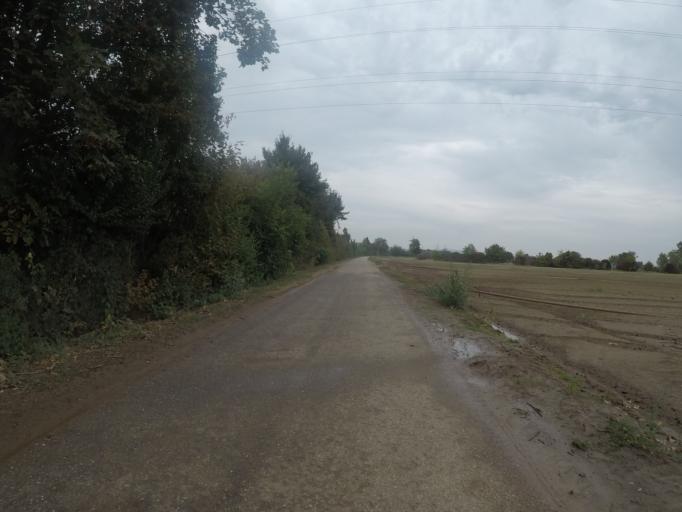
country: DE
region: Rheinland-Pfalz
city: Hassloch
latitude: 49.3761
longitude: 8.2594
